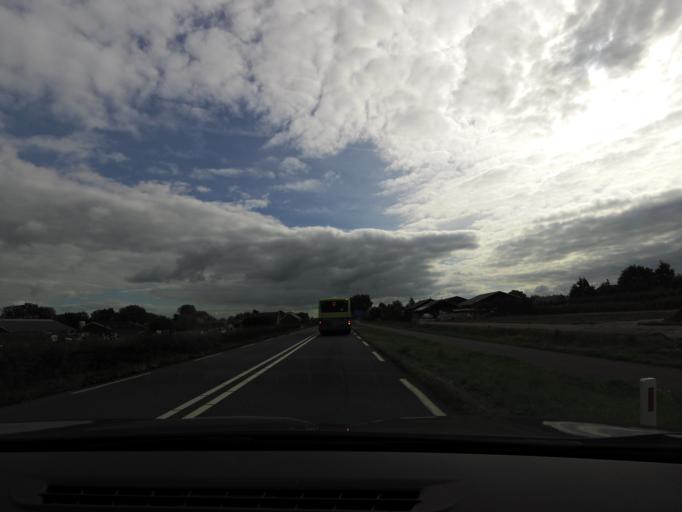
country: NL
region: Utrecht
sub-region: Gemeente Lopik
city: Lopik
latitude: 51.9821
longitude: 4.9760
